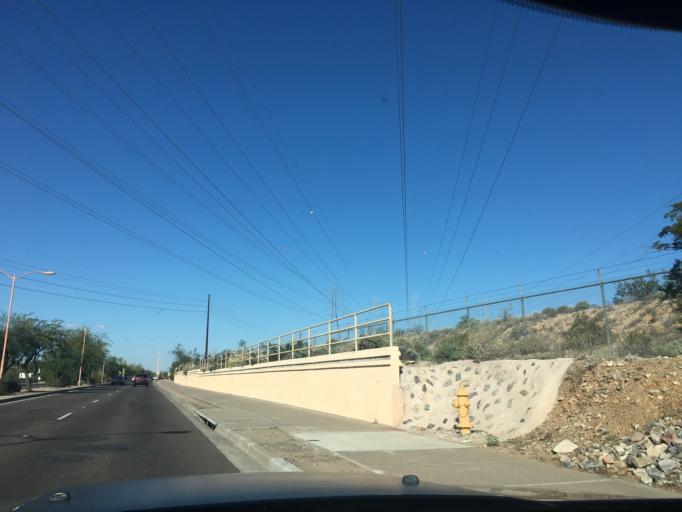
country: US
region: Arizona
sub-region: Maricopa County
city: Scottsdale
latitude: 33.5990
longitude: -111.8450
